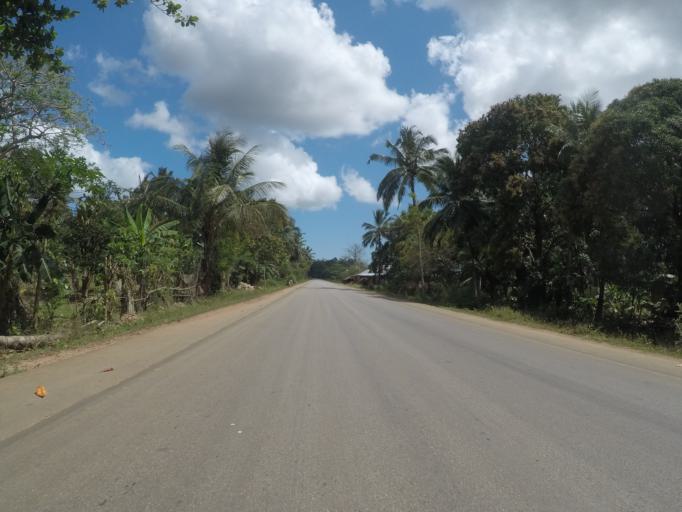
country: TZ
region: Zanzibar Central/South
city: Koani
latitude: -6.1788
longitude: 39.3287
